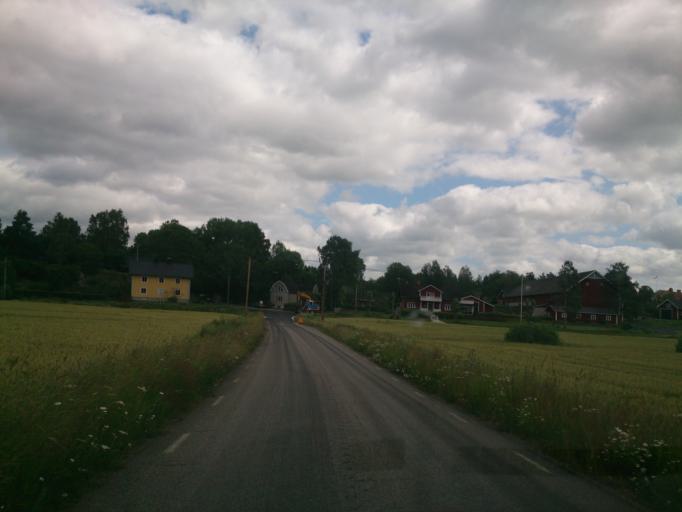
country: SE
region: OEstergoetland
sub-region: Norrkopings Kommun
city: Krokek
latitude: 58.5071
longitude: 16.5991
